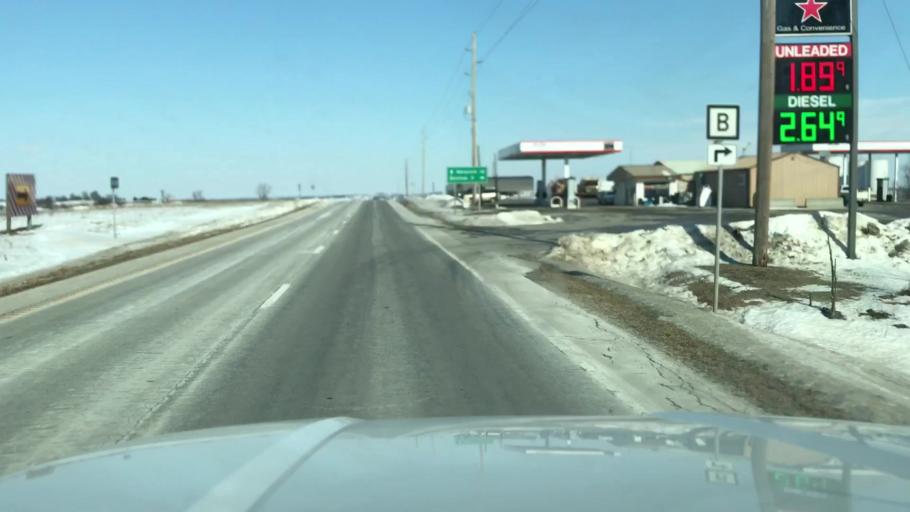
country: US
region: Missouri
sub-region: Andrew County
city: Savannah
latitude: 40.1125
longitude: -94.8697
